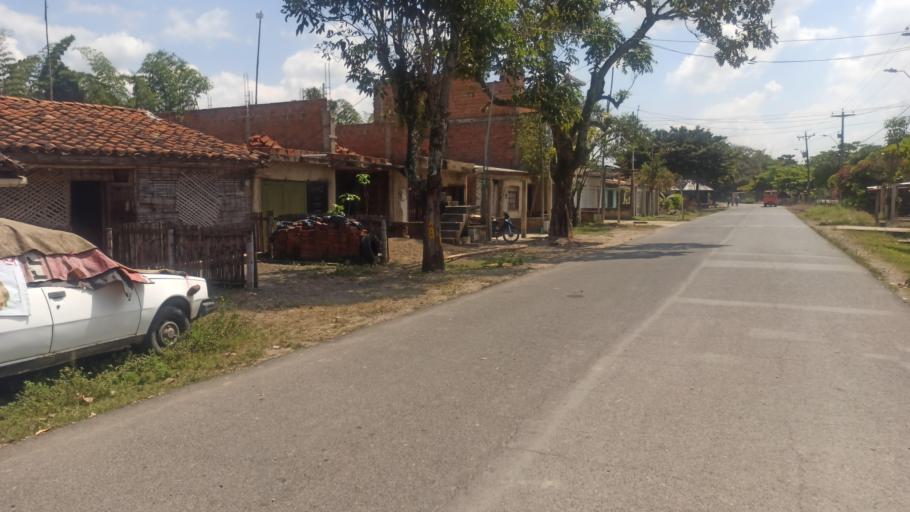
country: CO
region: Valle del Cauca
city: Jamundi
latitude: 3.1357
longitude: -76.5443
